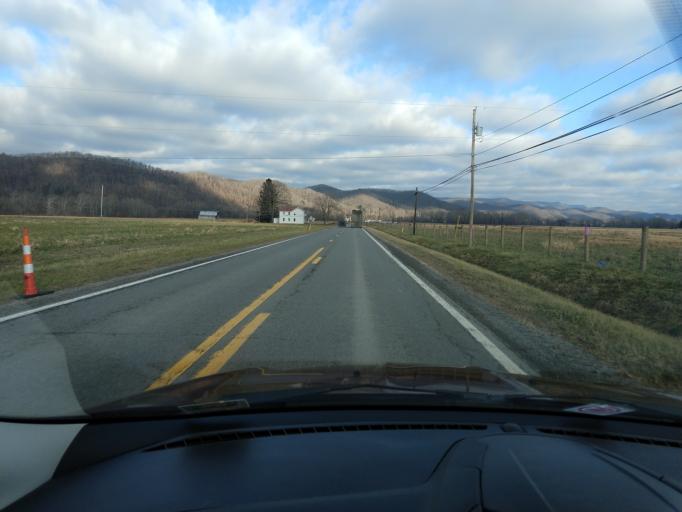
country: US
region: West Virginia
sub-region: Randolph County
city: Elkins
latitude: 38.6973
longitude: -79.9753
